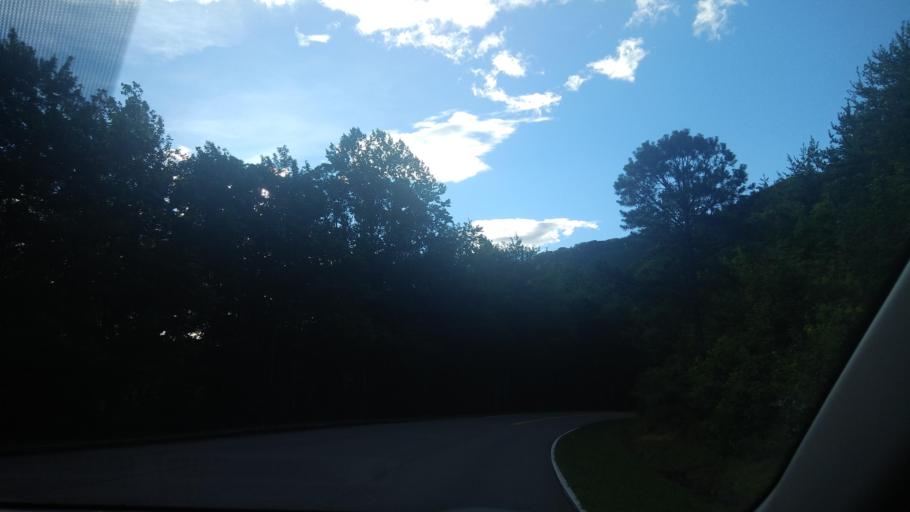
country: US
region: Tennessee
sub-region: Cocke County
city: Newport
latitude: 35.8249
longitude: -83.2099
